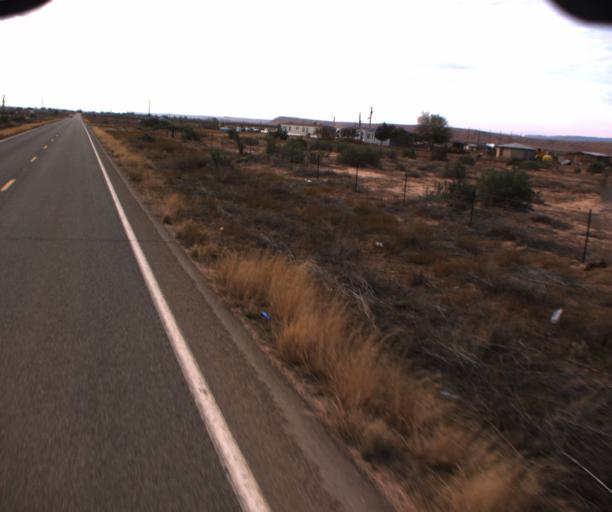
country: US
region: Arizona
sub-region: Apache County
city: Many Farms
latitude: 36.4402
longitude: -109.6073
